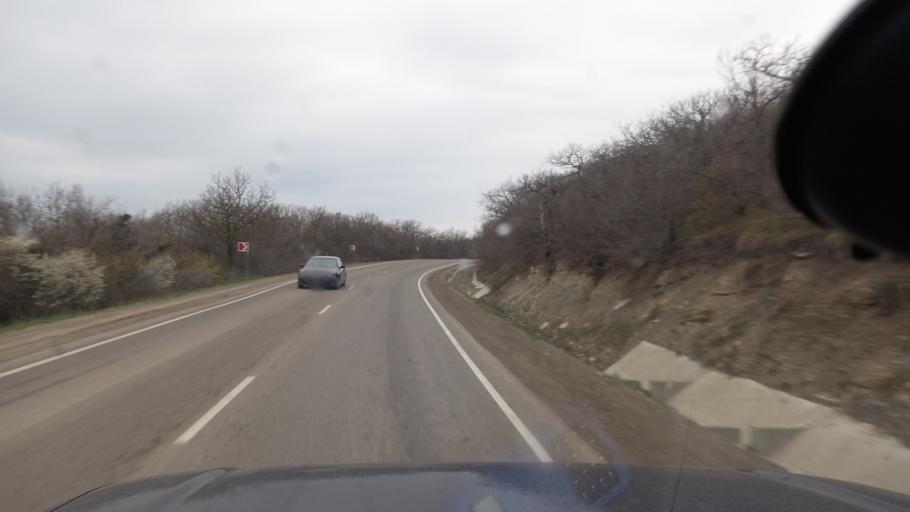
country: RU
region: Krasnodarskiy
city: Sukko
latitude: 44.8399
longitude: 37.4181
